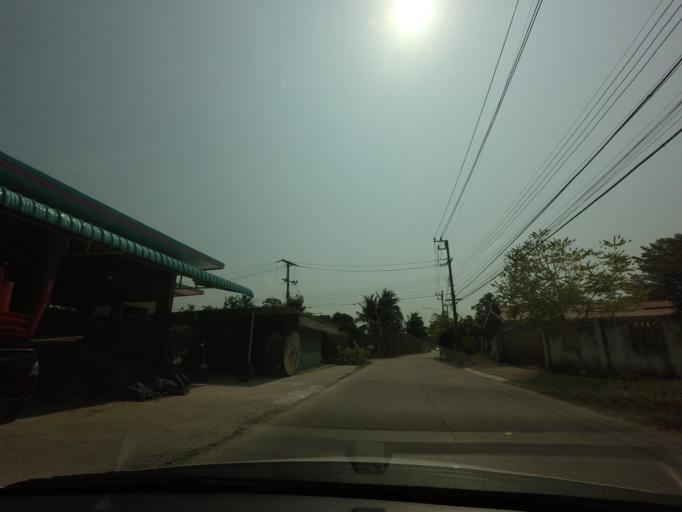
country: TH
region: Nakhon Pathom
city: Sam Phran
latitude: 13.7617
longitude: 100.2603
